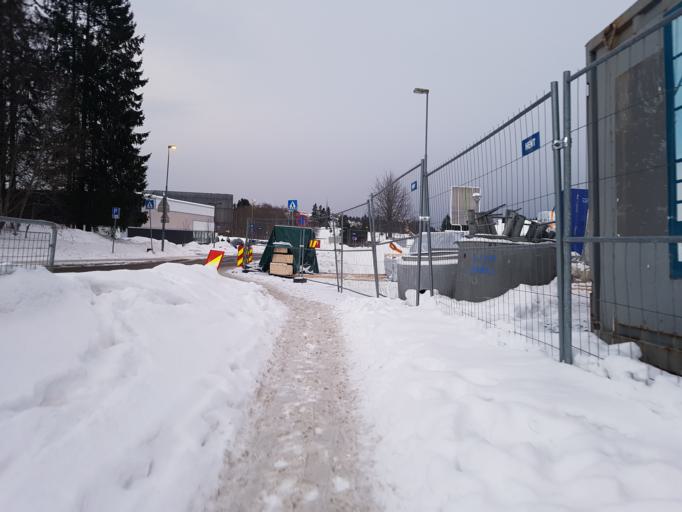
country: NO
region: Sor-Trondelag
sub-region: Trondheim
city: Trondheim
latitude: 63.3817
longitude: 10.3784
